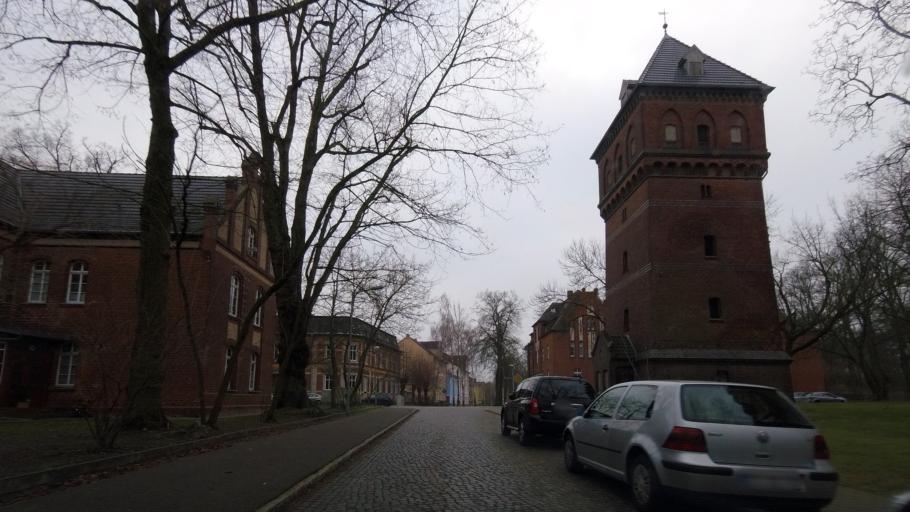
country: DE
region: Brandenburg
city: Juterbog
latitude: 51.9996
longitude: 13.0494
